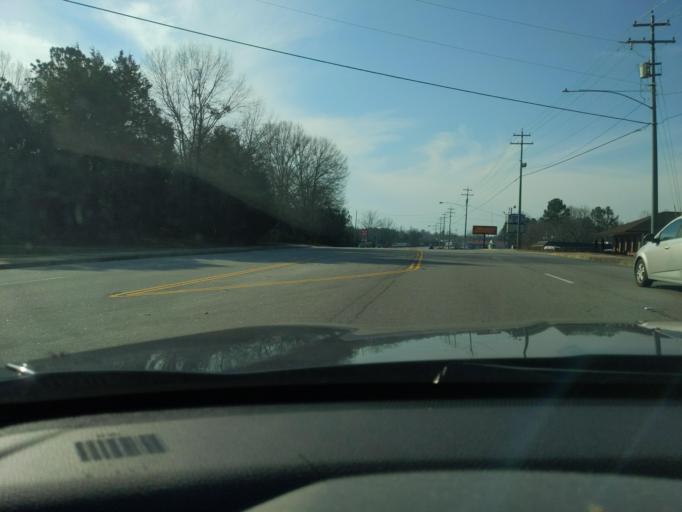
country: US
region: South Carolina
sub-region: Abbeville County
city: Abbeville
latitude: 34.1668
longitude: -82.3816
